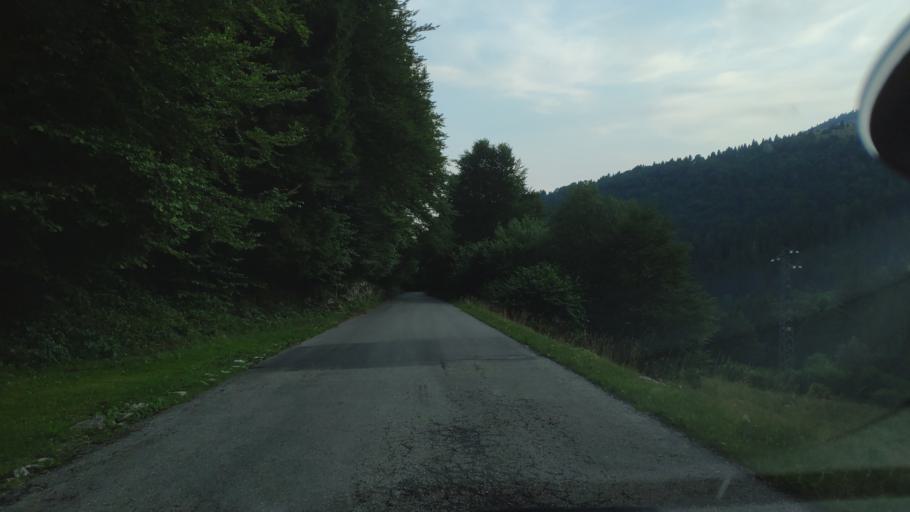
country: IT
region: Veneto
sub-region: Provincia di Vicenza
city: Calvene
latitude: 45.7973
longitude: 11.5078
